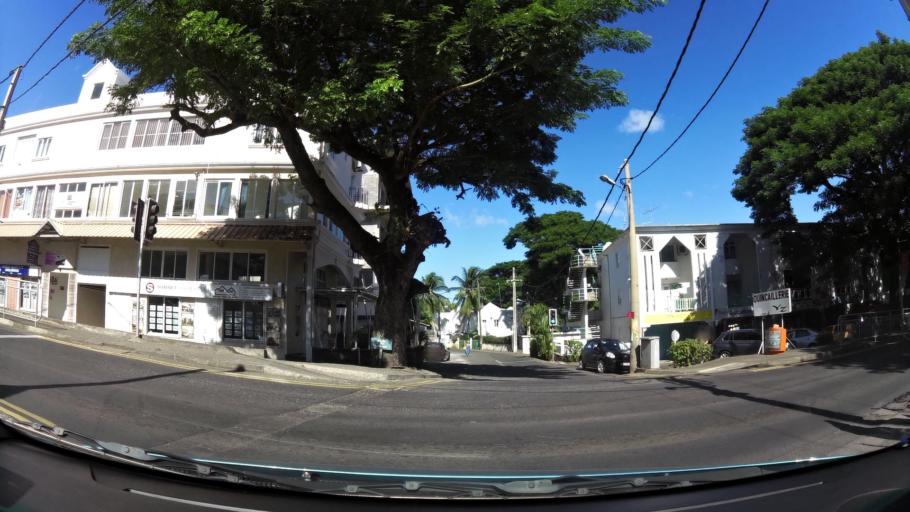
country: MU
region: Black River
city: Flic en Flac
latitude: -20.2760
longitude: 57.3719
